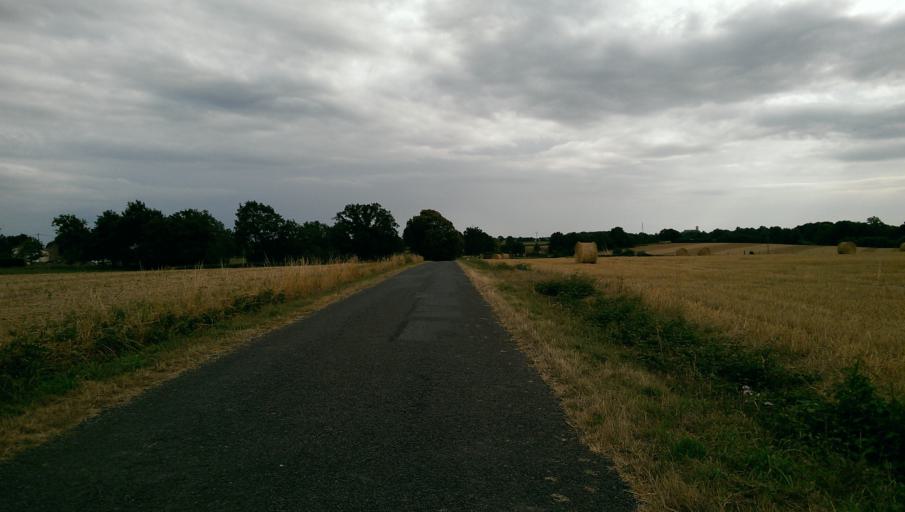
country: FR
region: Pays de la Loire
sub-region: Departement de la Loire-Atlantique
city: Vieillevigne
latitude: 46.9932
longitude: -1.4205
